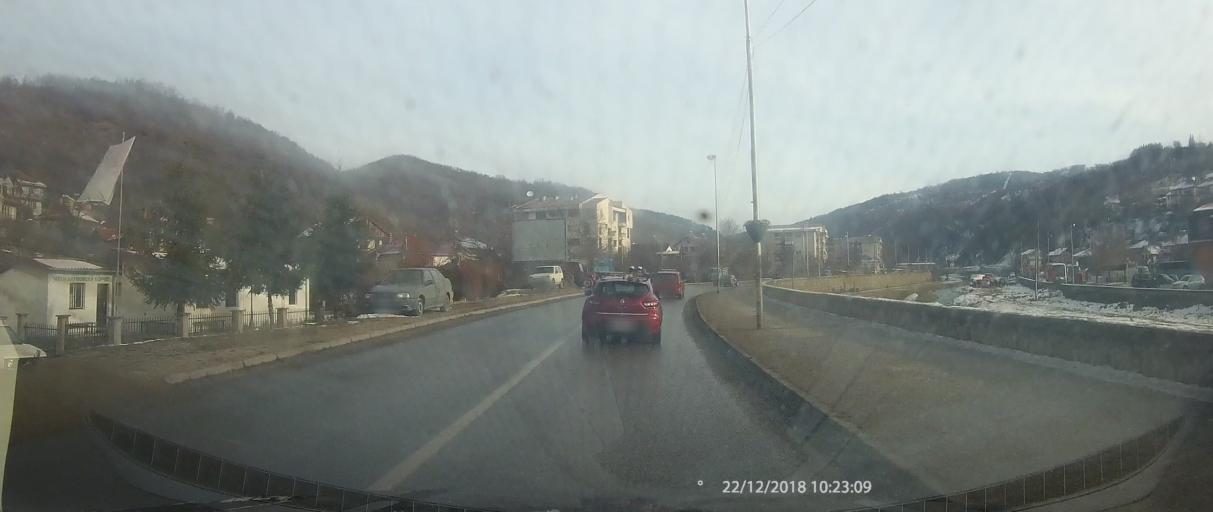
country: MK
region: Kriva Palanka
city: Kriva Palanka
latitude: 42.2070
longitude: 22.3348
